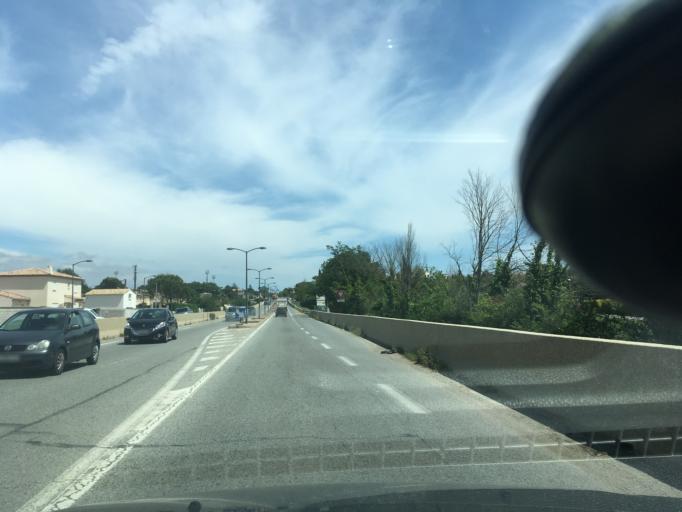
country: FR
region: Provence-Alpes-Cote d'Azur
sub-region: Departement du Var
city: Puget-sur-Argens
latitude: 43.4580
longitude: 6.6775
